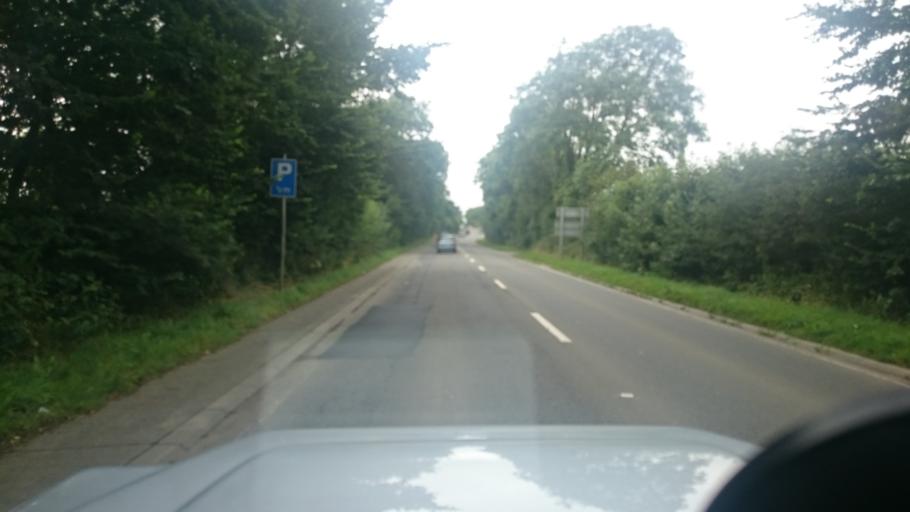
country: GB
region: Wales
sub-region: Pembrokeshire
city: Haverfordwest
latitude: 51.8190
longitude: -4.9636
